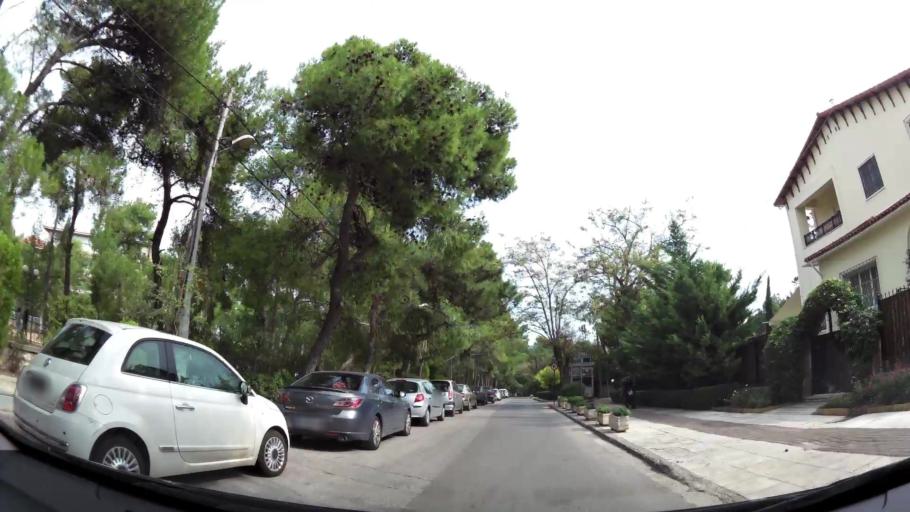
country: GR
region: Attica
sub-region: Nomarchia Athinas
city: Psychiko
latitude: 38.0111
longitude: 23.7758
